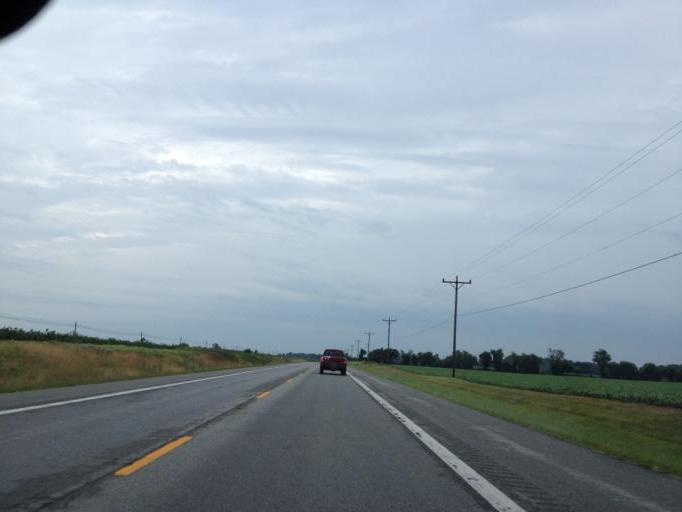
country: US
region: Maryland
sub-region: Queen Anne's County
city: Centreville
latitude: 38.9367
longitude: -76.0488
